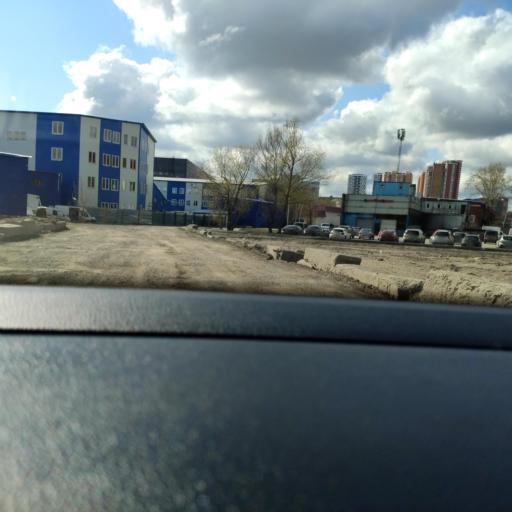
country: RU
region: Moscow
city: Kotlovka
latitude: 55.6785
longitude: 37.6163
